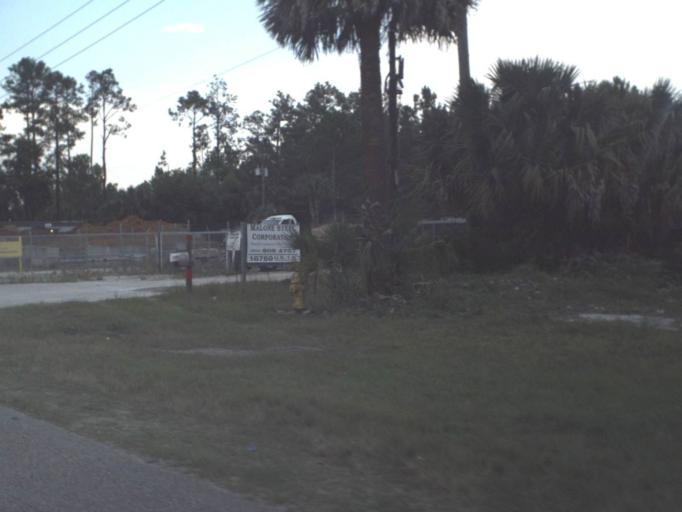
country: US
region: Florida
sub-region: Saint Johns County
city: Palm Valley
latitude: 30.0834
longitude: -81.4572
